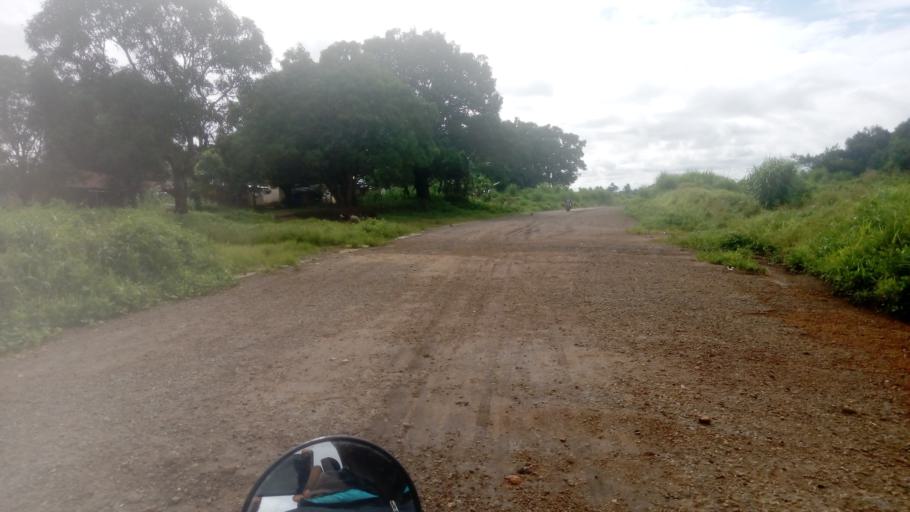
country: SL
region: Northern Province
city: Port Loko
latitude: 8.7108
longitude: -12.6789
